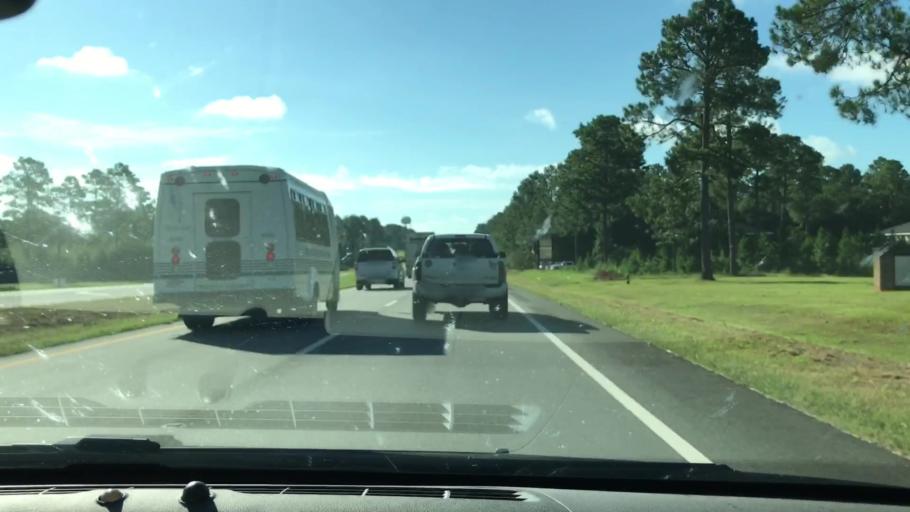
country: US
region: Georgia
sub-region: Lee County
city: Leesburg
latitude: 31.6469
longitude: -84.2598
